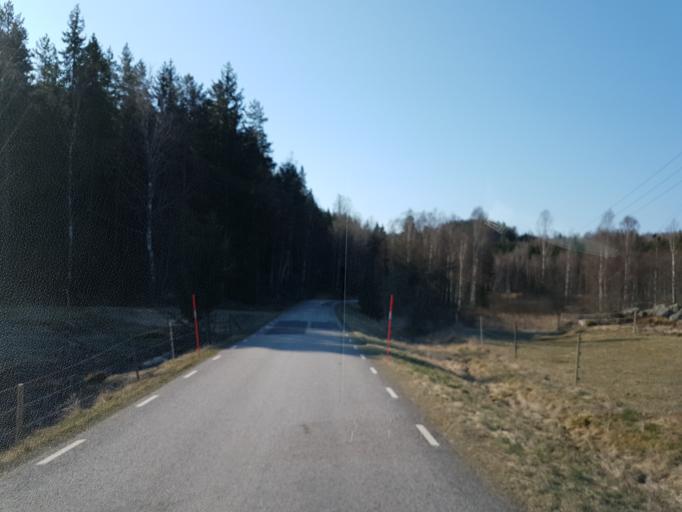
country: SE
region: Kalmar
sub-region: Vasterviks Kommun
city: Overum
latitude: 58.1862
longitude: 16.2811
